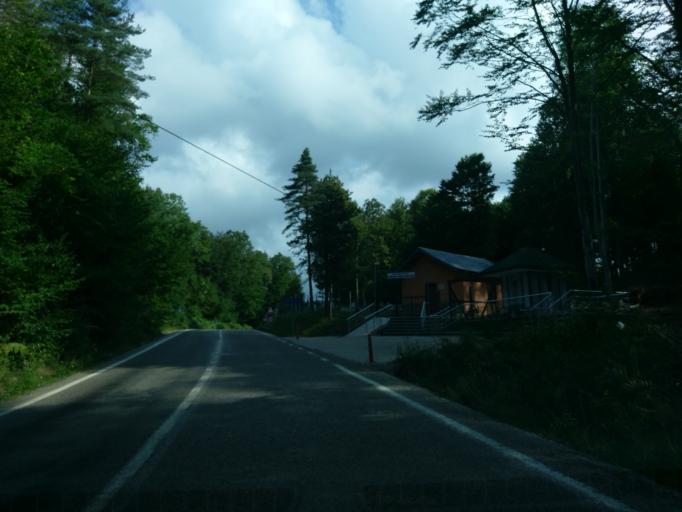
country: TR
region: Sinop
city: Ayancik
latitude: 41.8806
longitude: 34.5137
